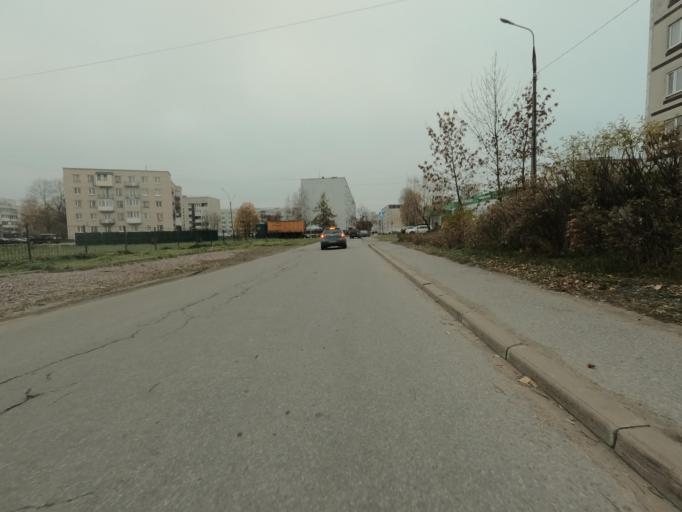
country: RU
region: Leningrad
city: Kirovsk
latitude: 59.8816
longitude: 30.9960
